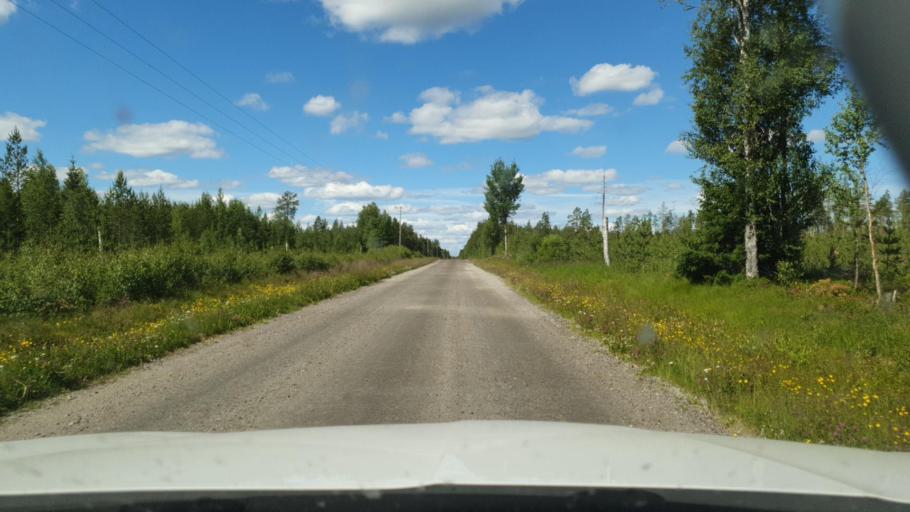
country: SE
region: Vaesterbotten
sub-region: Skelleftea Kommun
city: Backa
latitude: 65.1641
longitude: 21.1377
